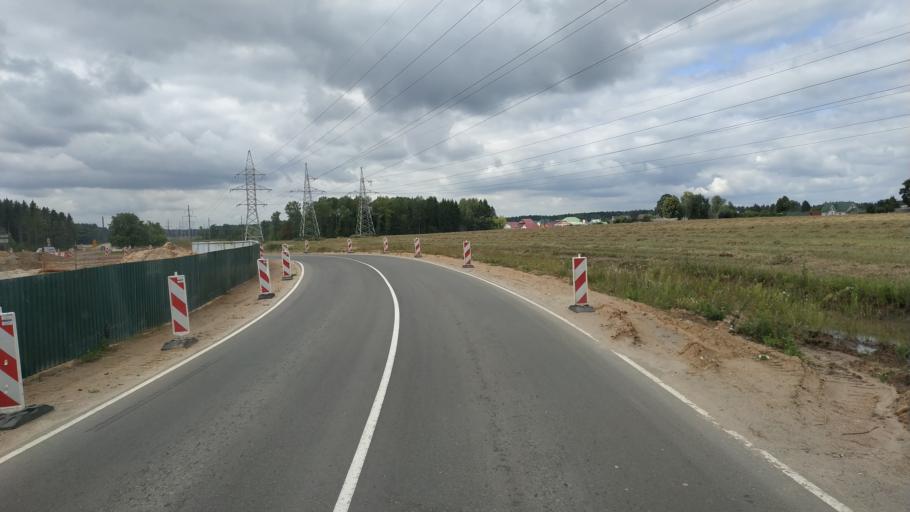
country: BY
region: Mogilev
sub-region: Mahilyowski Rayon
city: Kadino
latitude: 53.8711
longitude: 30.4580
